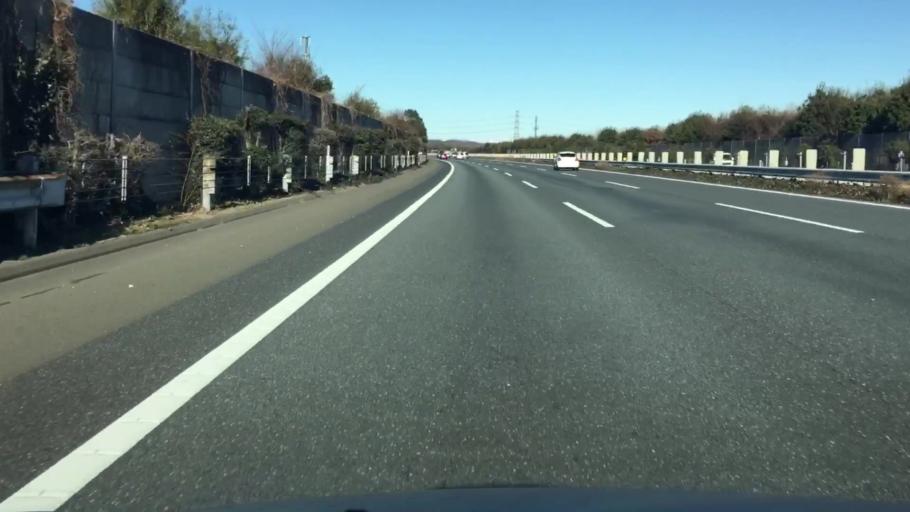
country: JP
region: Saitama
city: Honjo
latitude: 36.1939
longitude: 139.1879
